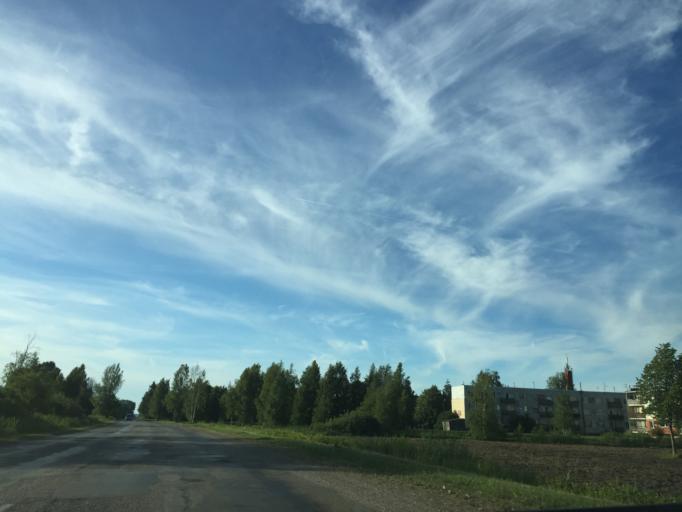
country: LV
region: Ventspils
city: Ventspils
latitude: 57.3022
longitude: 21.5609
